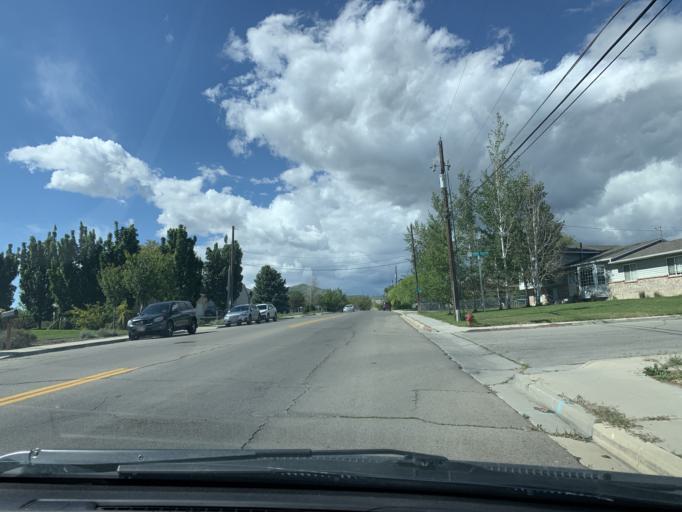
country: US
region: Utah
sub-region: Utah County
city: Lehi
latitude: 40.4021
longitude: -111.8398
